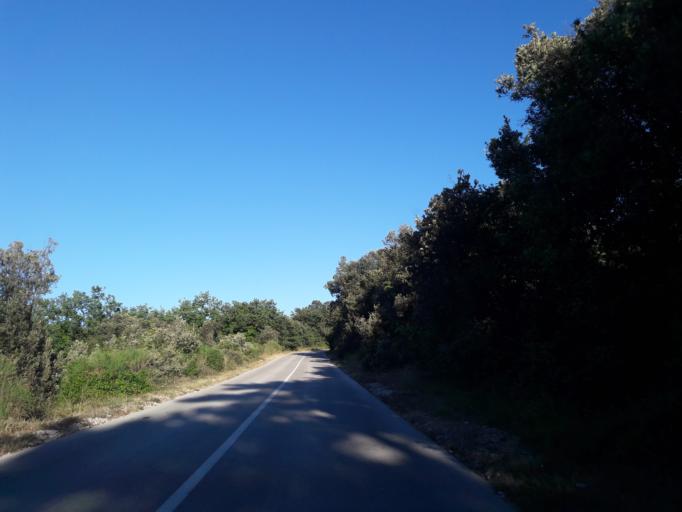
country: HR
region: Dubrovacko-Neretvanska
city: Orebic
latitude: 42.9999
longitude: 17.2563
